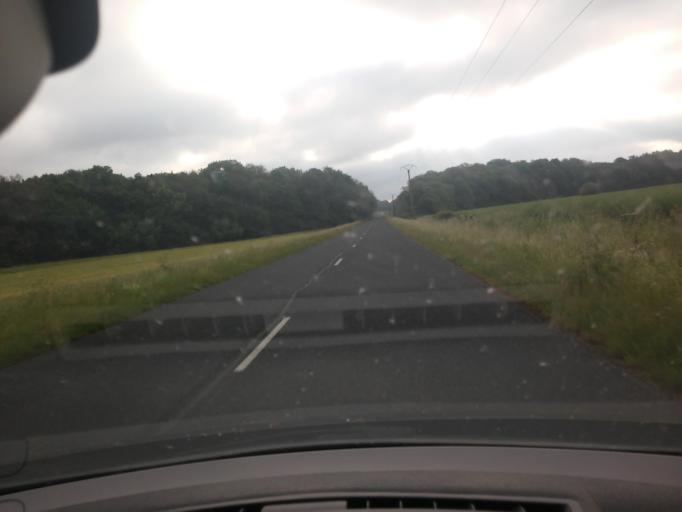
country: FR
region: Lorraine
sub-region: Departement de la Meuse
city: Vigneulles-les-Hattonchatel
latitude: 48.9807
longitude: 5.7492
